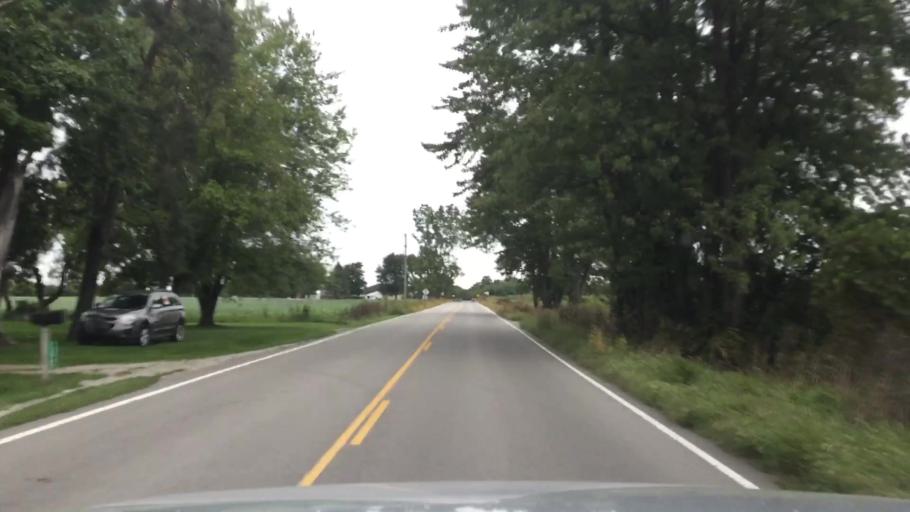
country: US
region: Michigan
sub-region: Washtenaw County
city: Milan
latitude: 42.0852
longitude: -83.7350
